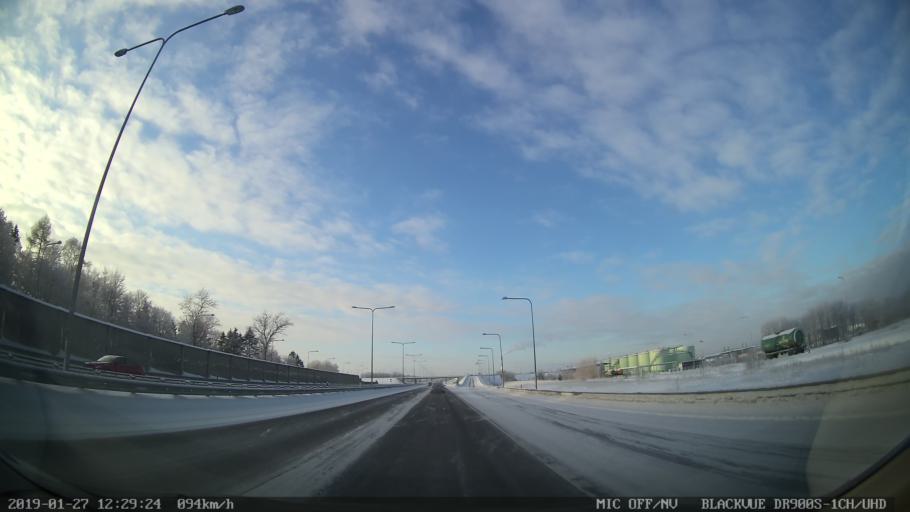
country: EE
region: Harju
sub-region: Maardu linn
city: Maardu
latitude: 59.4514
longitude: 24.9901
